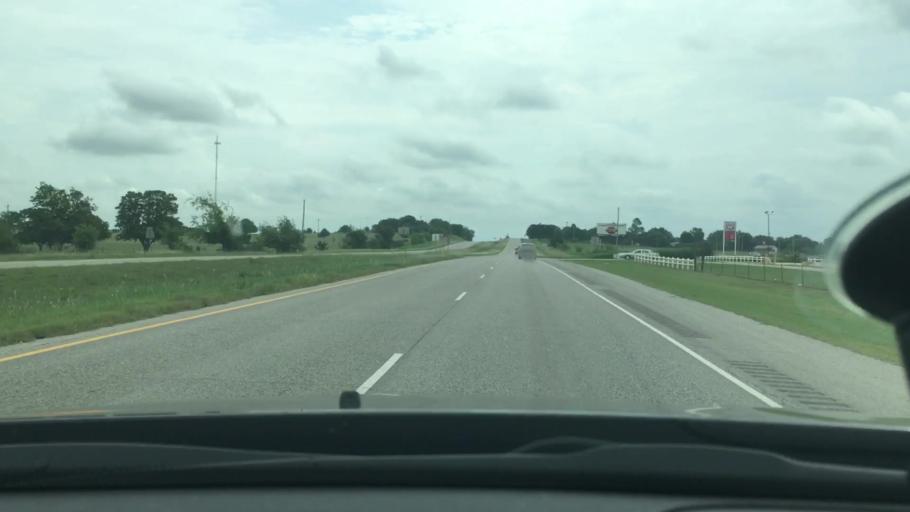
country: US
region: Oklahoma
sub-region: Carter County
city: Wilson
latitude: 34.1728
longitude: -97.4147
